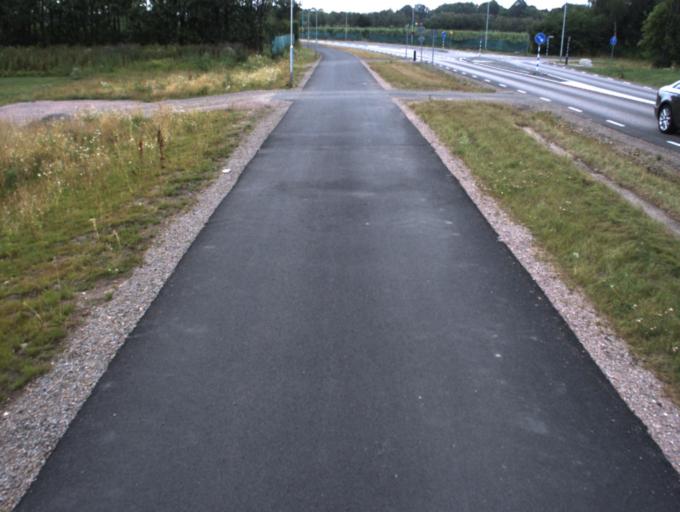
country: SE
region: Skane
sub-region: Helsingborg
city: Helsingborg
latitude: 56.0534
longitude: 12.7389
